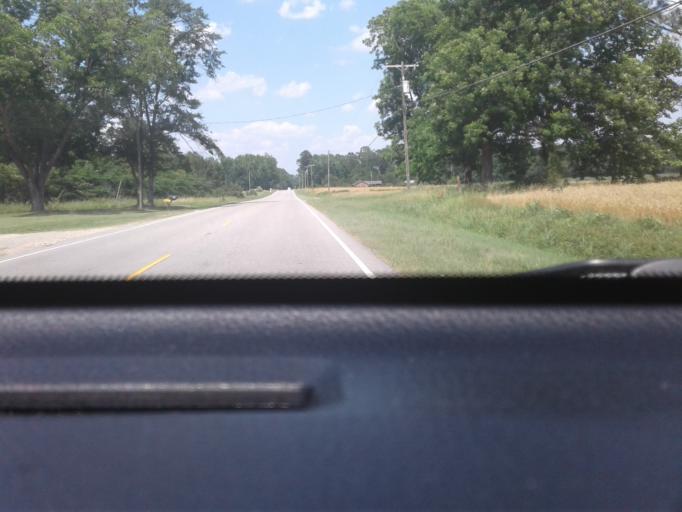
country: US
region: North Carolina
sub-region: Cumberland County
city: Eastover
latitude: 35.1292
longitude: -78.7557
